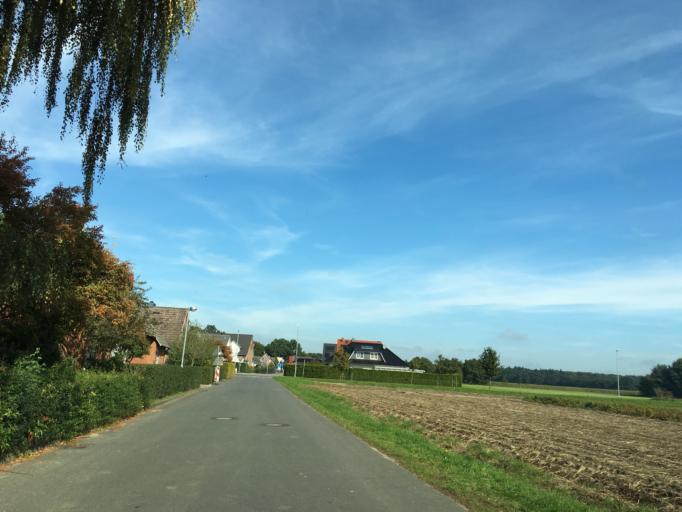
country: DE
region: Lower Saxony
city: Adendorf
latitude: 53.2774
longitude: 10.4661
